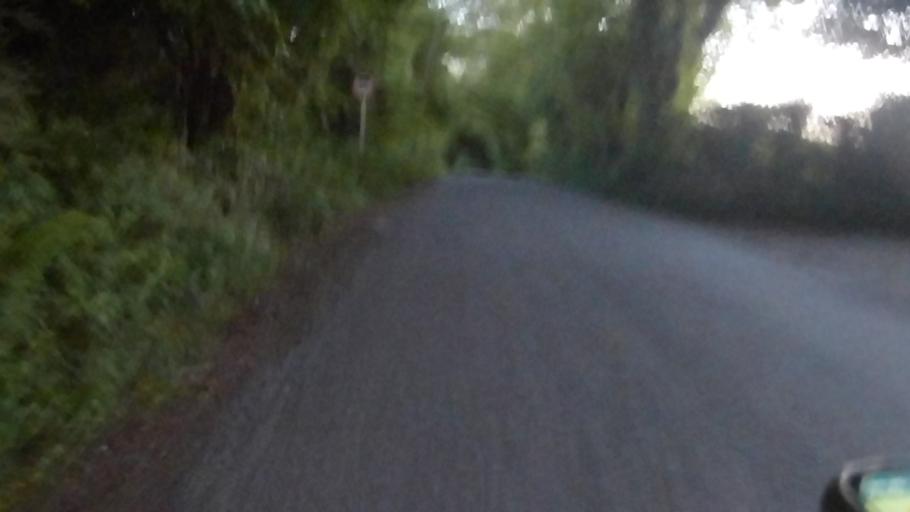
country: IE
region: Munster
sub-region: County Cork
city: Carrigtwohill
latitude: 51.9695
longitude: -8.2718
